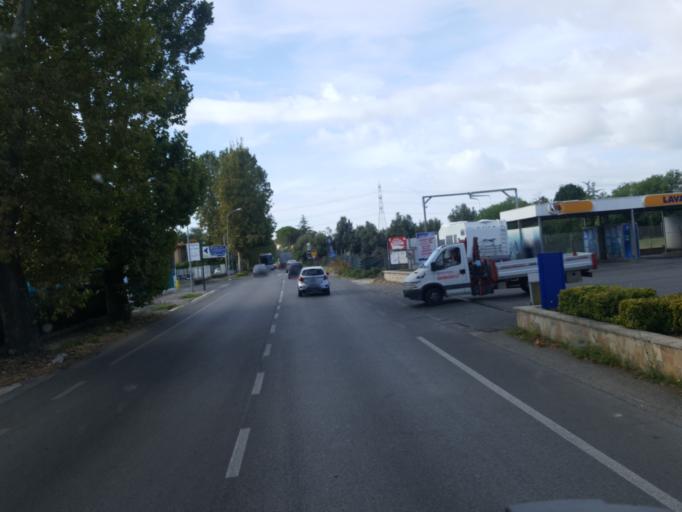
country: IT
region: Latium
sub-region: Citta metropolitana di Roma Capitale
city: Bivio di Capanelle
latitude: 42.1183
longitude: 12.5893
